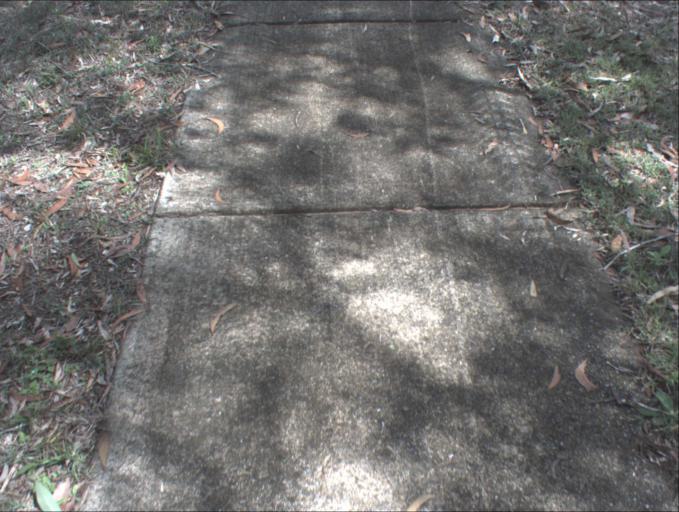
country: AU
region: Queensland
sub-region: Logan
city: North Maclean
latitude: -27.7450
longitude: 152.9480
